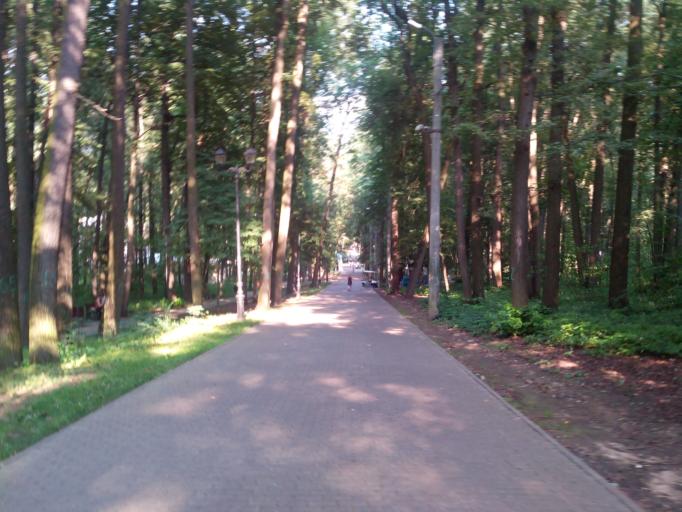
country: RU
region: Moskovskaya
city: Fili
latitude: 55.7506
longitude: 37.4816
